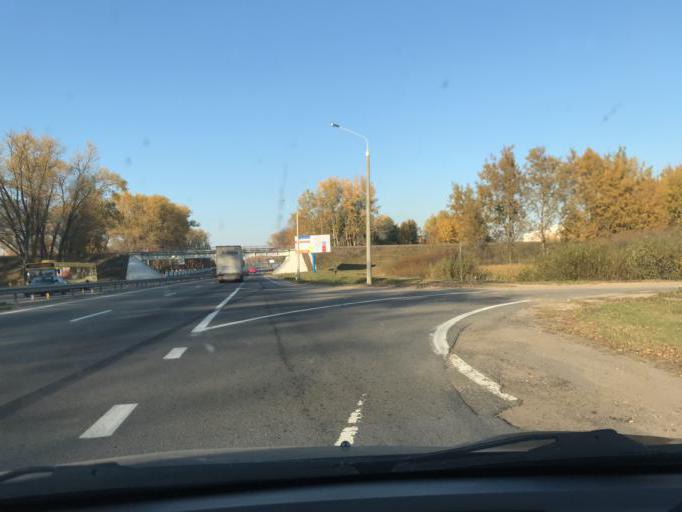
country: BY
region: Minsk
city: Yubilyeyny
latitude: 53.8129
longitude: 27.5301
